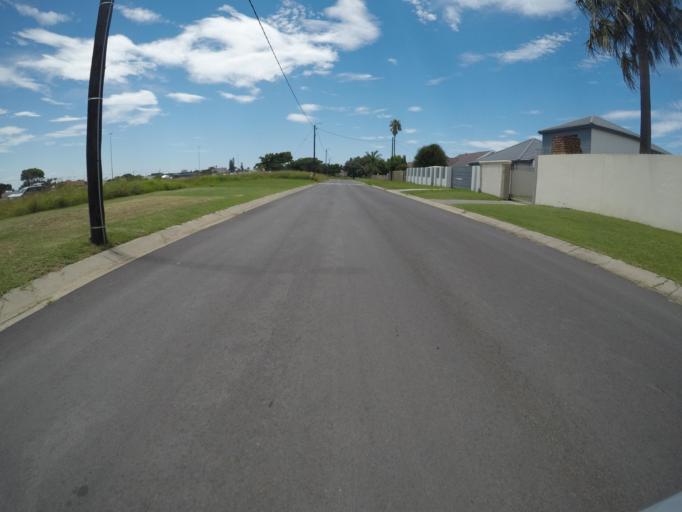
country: ZA
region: Eastern Cape
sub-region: Buffalo City Metropolitan Municipality
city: East London
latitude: -33.0362
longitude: 27.8516
